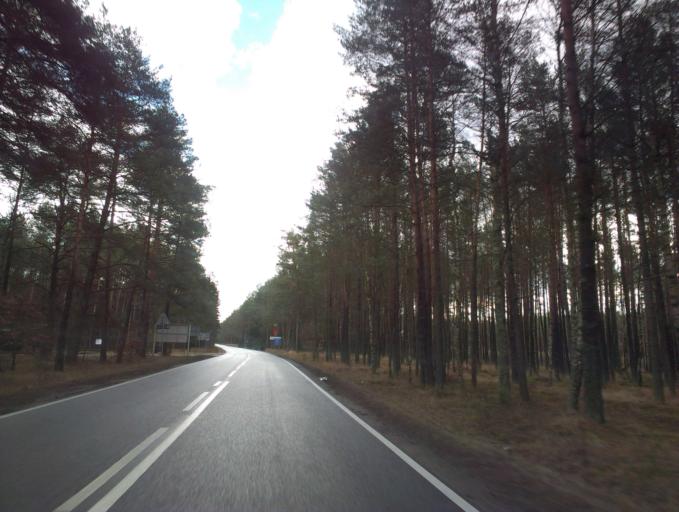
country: PL
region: Pomeranian Voivodeship
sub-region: Powiat czluchowski
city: Czarne
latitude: 53.7014
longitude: 16.8784
